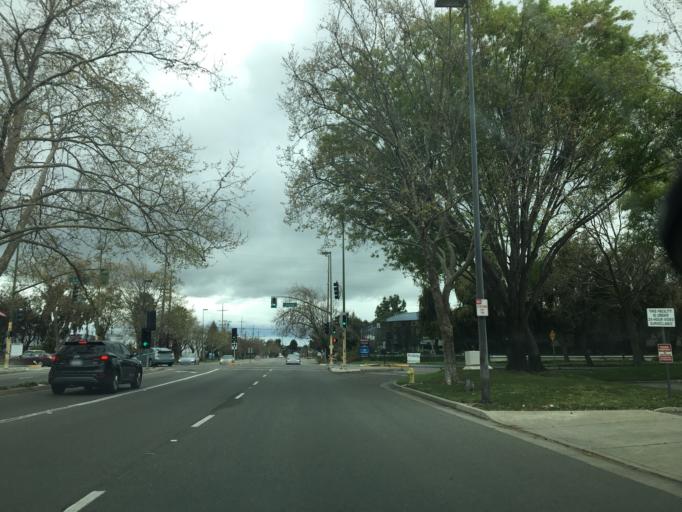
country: US
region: California
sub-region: Santa Clara County
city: Milpitas
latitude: 37.4033
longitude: -121.8898
